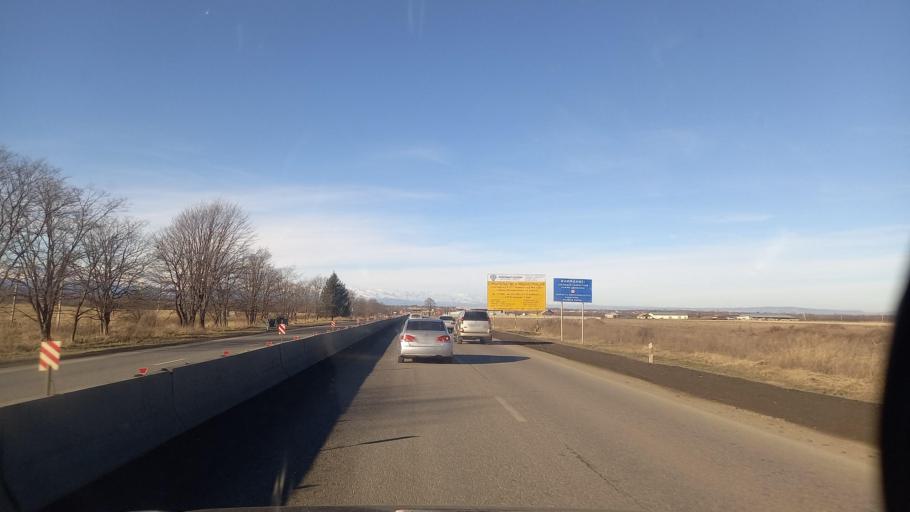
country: RU
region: North Ossetia
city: Vladikavkaz
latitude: 43.0257
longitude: 44.6241
